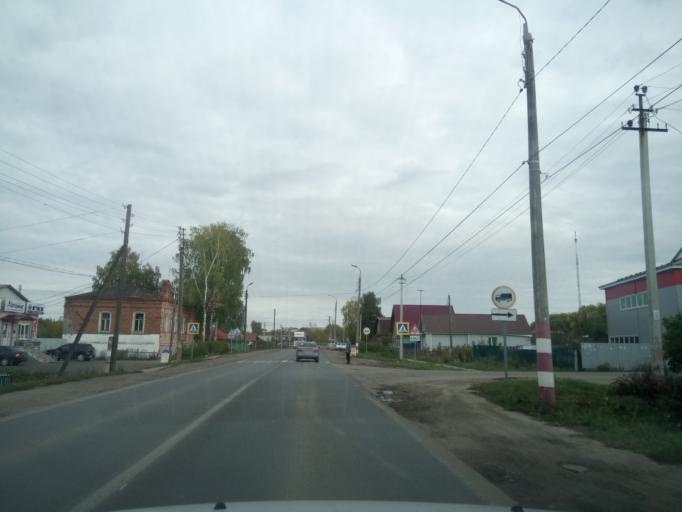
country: RU
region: Nizjnij Novgorod
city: Lukoyanov
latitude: 55.0304
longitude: 44.4868
